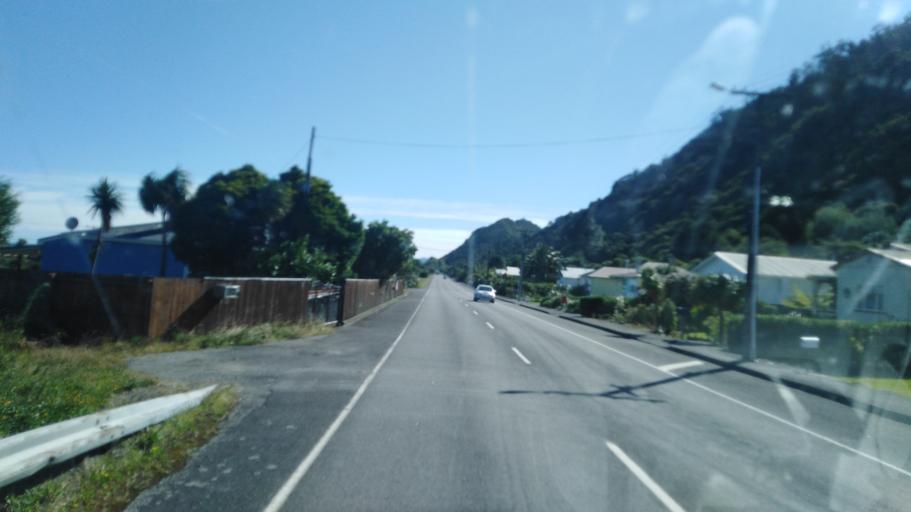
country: NZ
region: West Coast
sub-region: Buller District
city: Westport
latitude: -41.6372
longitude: 171.8476
